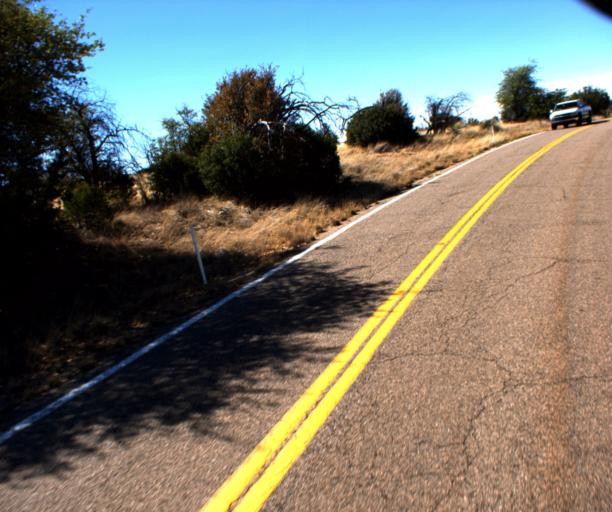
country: US
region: Arizona
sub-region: Cochise County
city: Huachuca City
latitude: 31.5541
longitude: -110.5503
